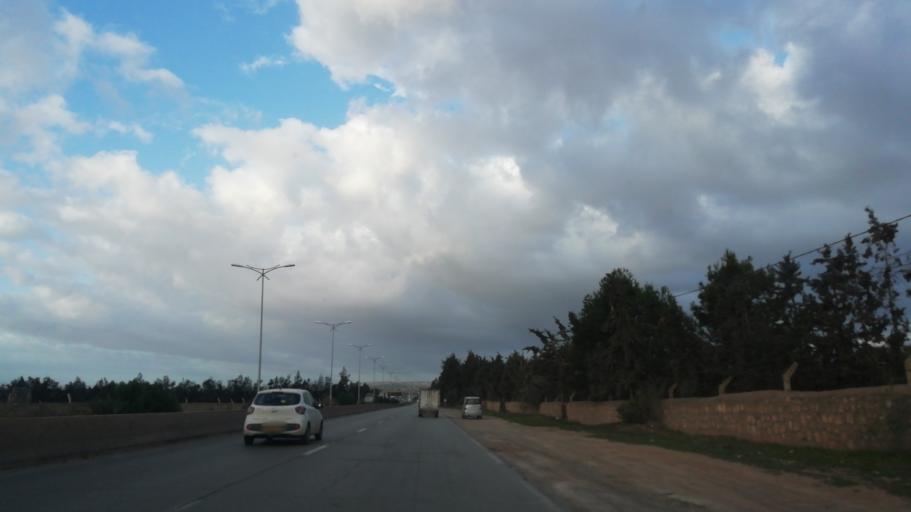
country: DZ
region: Oran
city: Bou Tlelis
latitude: 35.5728
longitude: -0.8645
